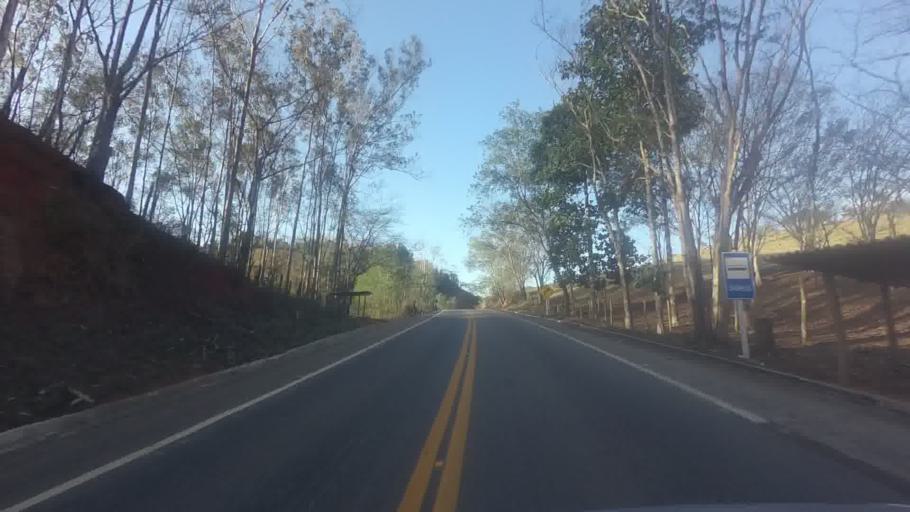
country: BR
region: Espirito Santo
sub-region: Cachoeiro De Itapemirim
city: Cachoeiro de Itapemirim
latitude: -20.8759
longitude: -41.2652
